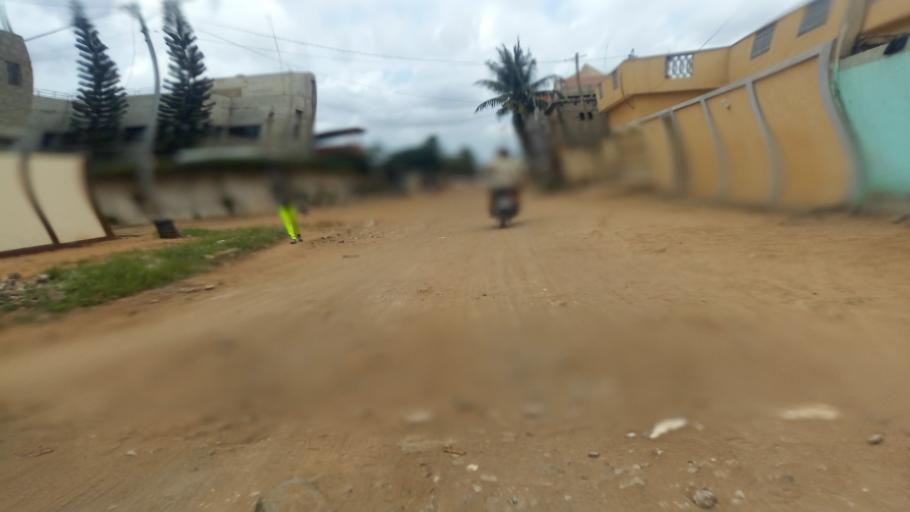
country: TG
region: Maritime
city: Lome
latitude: 6.2260
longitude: 1.1900
